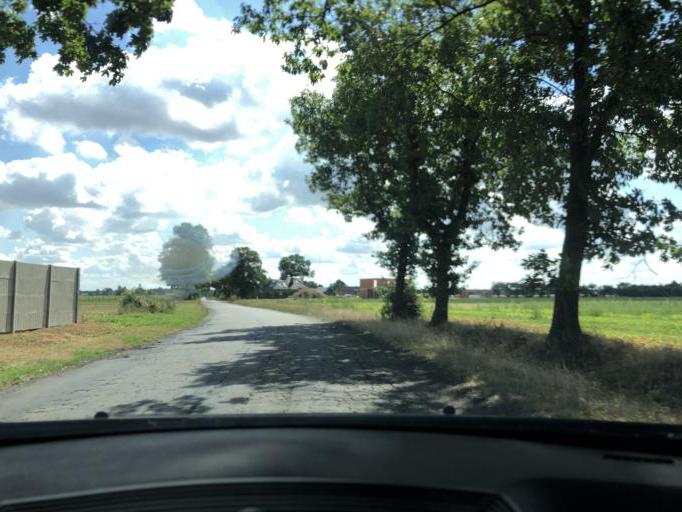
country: PL
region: Lodz Voivodeship
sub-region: Powiat wieruszowski
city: Czastary
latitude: 51.2385
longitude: 18.3386
